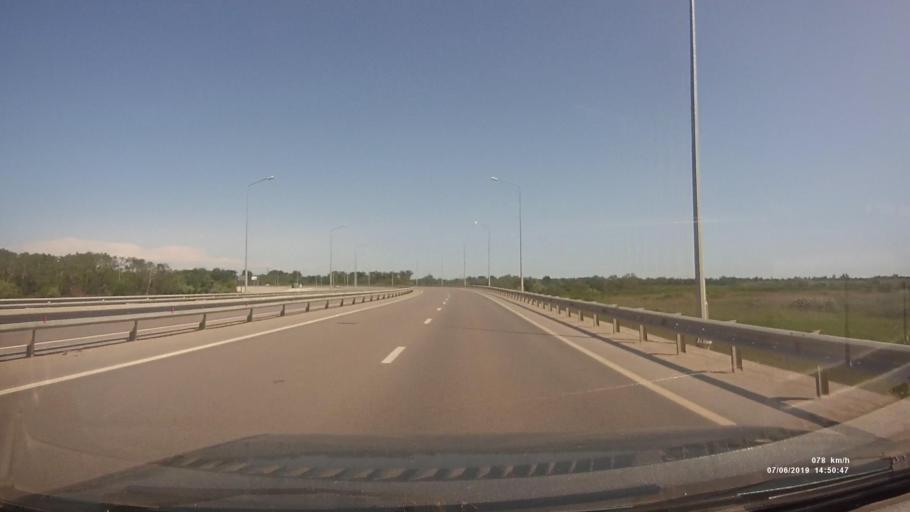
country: RU
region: Rostov
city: Rostov-na-Donu
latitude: 47.2059
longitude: 39.7527
